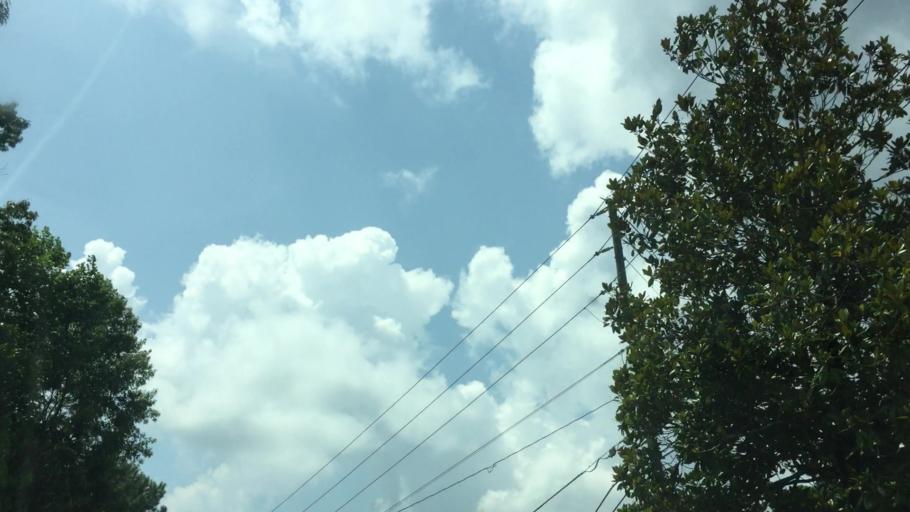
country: US
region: Georgia
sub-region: Carroll County
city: Villa Rica
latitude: 33.6147
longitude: -84.8843
